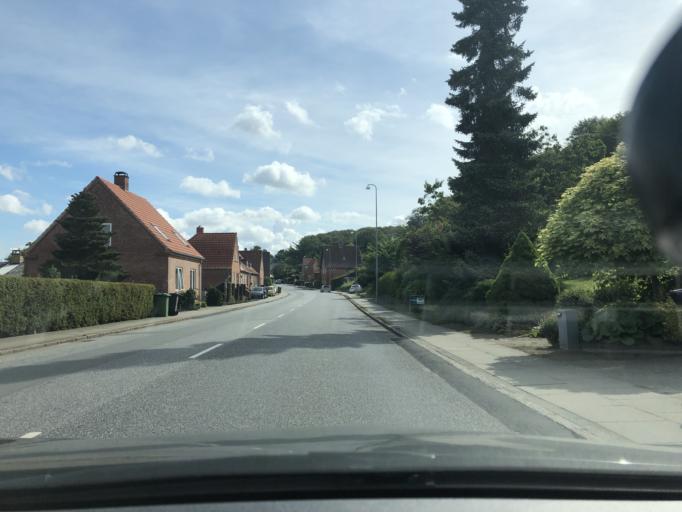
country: DK
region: South Denmark
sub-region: Vejle Kommune
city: Vejle
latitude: 55.7001
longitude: 9.5107
